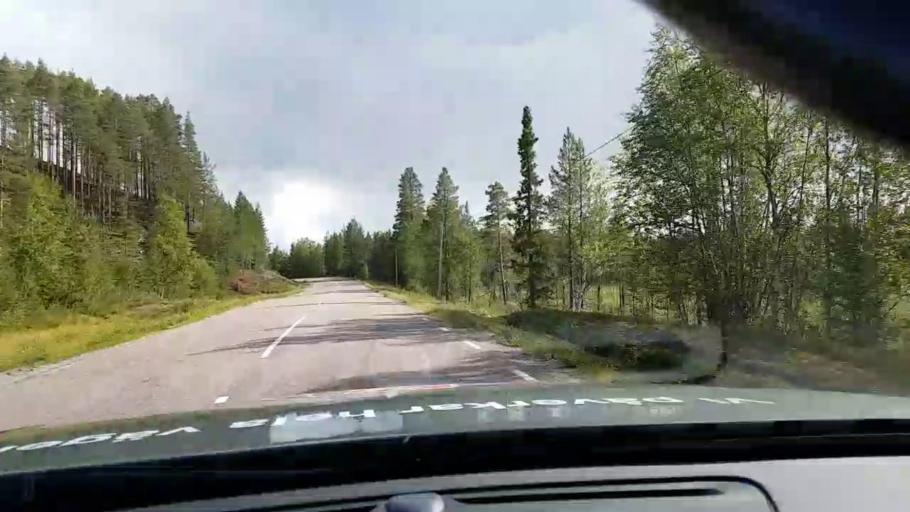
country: SE
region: Vaesterbotten
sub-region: Asele Kommun
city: Asele
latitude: 63.8674
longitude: 17.3602
